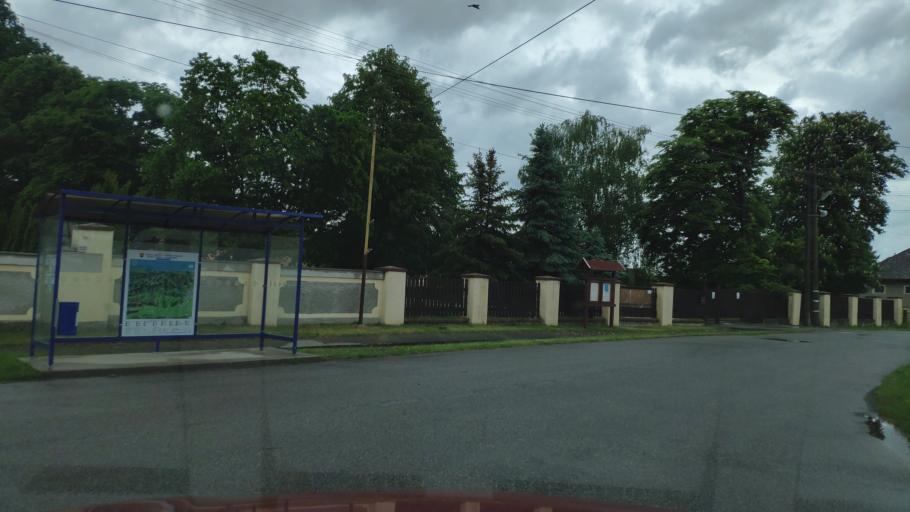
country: SK
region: Kosicky
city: Moldava nad Bodvou
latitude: 48.5396
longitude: 21.1092
